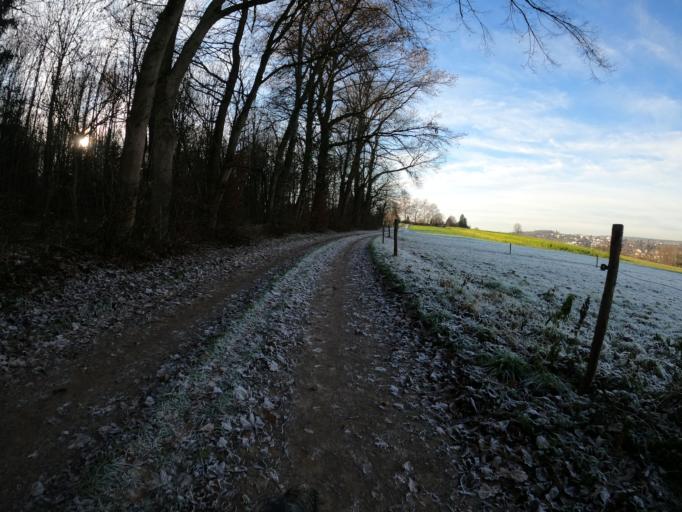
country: DE
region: Baden-Wuerttemberg
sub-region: Regierungsbezirk Stuttgart
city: Goeppingen
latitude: 48.7050
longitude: 9.6293
